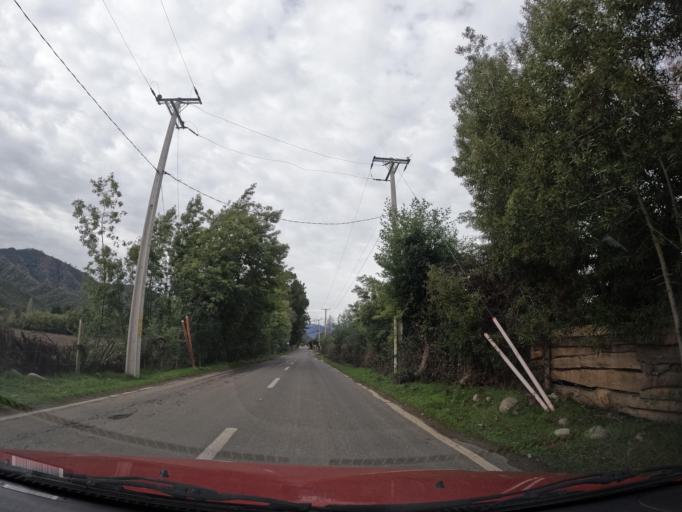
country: CL
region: Maule
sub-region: Provincia de Linares
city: Linares
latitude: -35.9232
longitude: -71.4073
